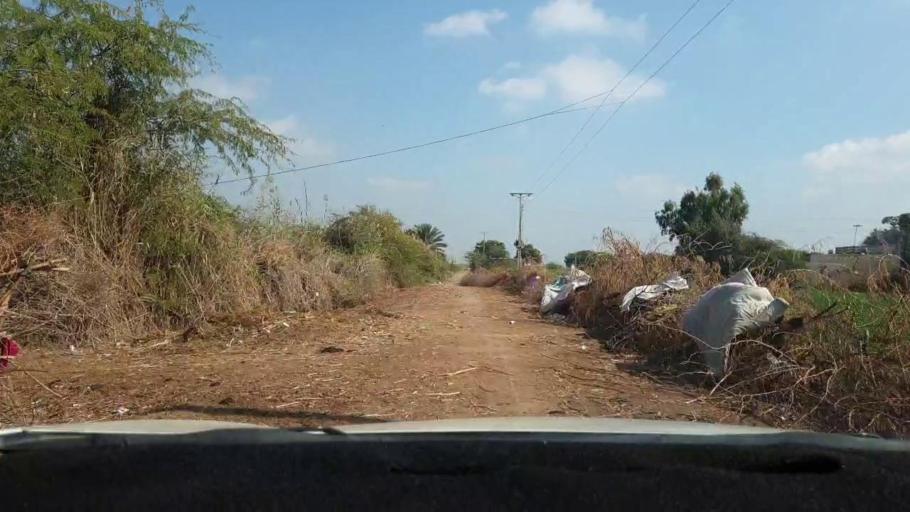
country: PK
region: Sindh
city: Berani
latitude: 25.7622
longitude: 68.8679
